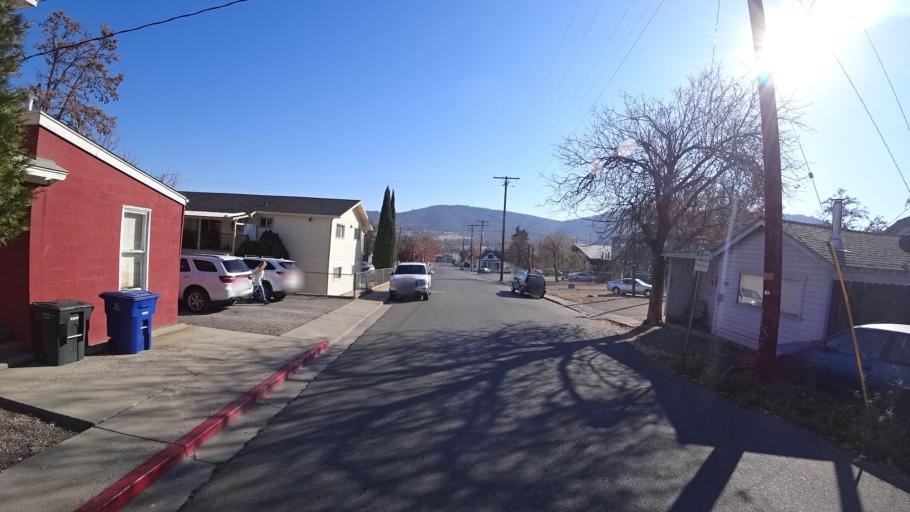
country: US
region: California
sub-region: Siskiyou County
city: Yreka
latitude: 41.7331
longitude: -122.6378
